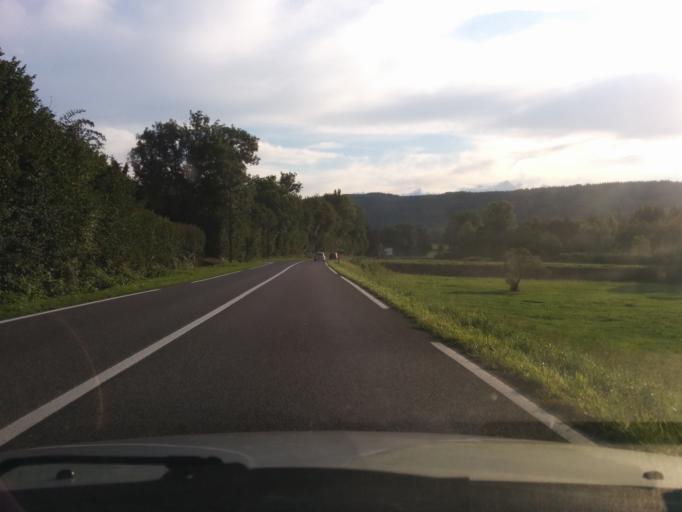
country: FR
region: Rhone-Alpes
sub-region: Departement de l'Isere
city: Saint-Joseph-de-Riviere
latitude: 45.3729
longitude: 5.6951
